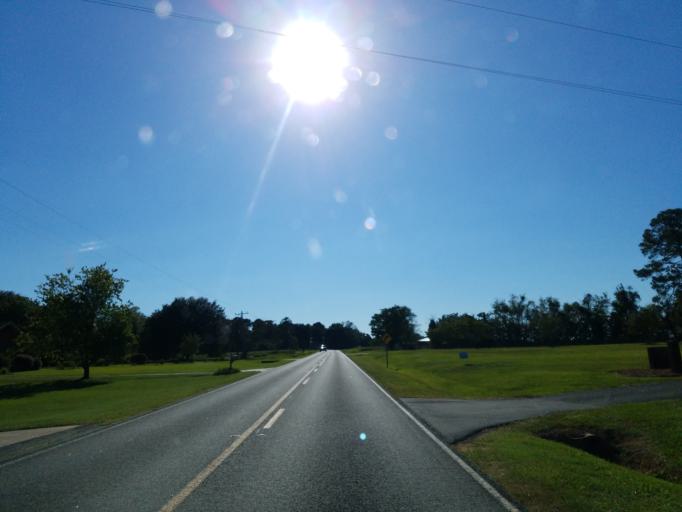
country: US
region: Georgia
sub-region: Dooly County
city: Unadilla
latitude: 32.2596
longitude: -83.7556
